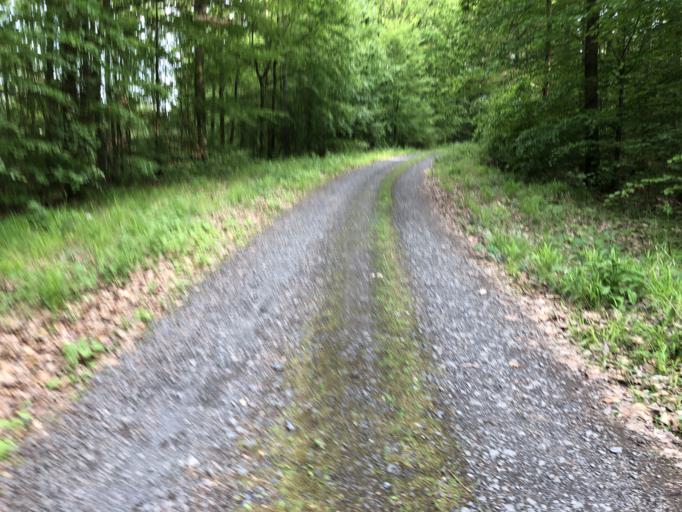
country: DE
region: Bavaria
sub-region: Upper Franconia
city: Memmelsdorf
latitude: 49.9172
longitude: 10.9566
